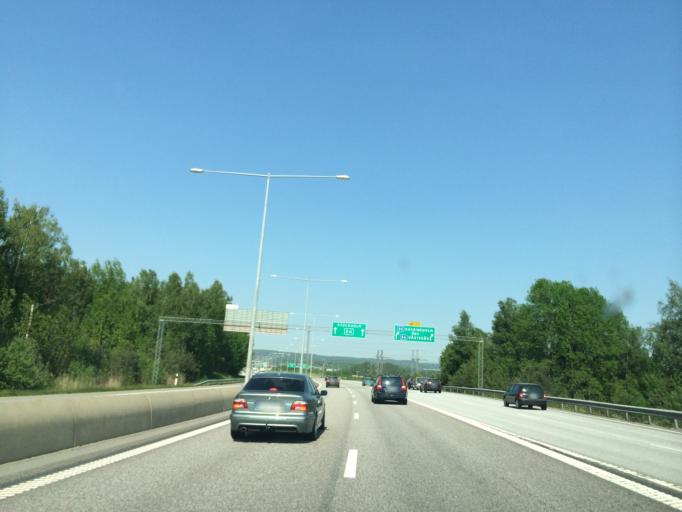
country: SE
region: OEstergoetland
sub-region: Norrkopings Kommun
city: Jursla
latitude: 58.6343
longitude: 16.1598
